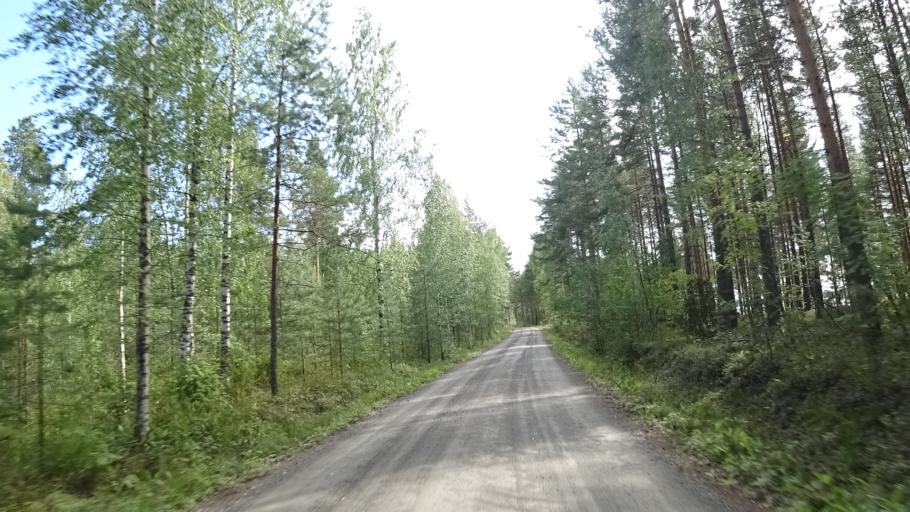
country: FI
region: North Karelia
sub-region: Joensuu
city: Pyhaeselkae
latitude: 62.3855
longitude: 29.7989
